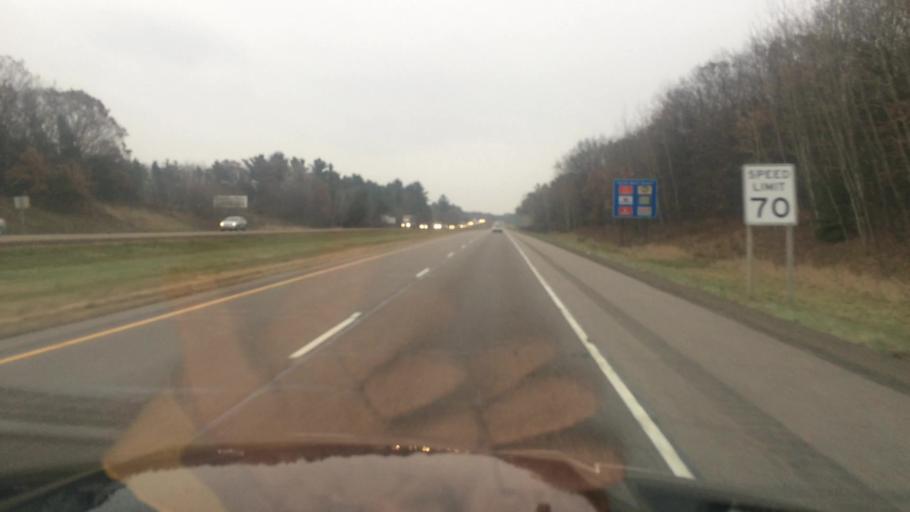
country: US
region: Wisconsin
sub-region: Portage County
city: Stevens Point
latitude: 44.5620
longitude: -89.5919
